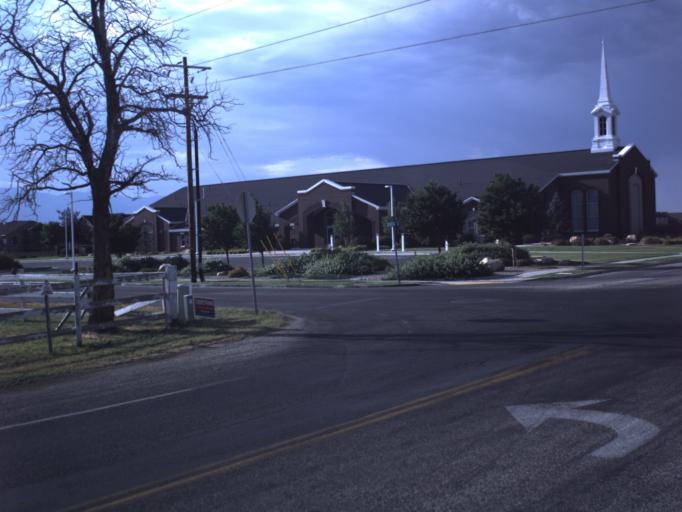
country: US
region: Utah
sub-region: Weber County
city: West Haven
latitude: 41.2057
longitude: -112.0930
